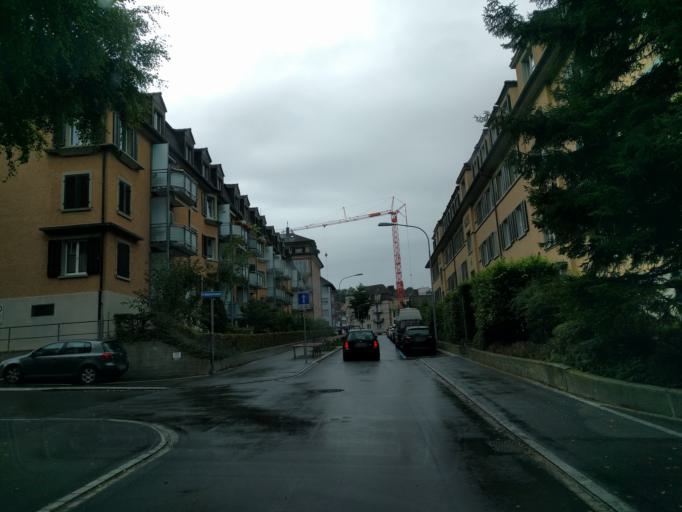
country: CH
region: Zurich
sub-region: Bezirk Zuerich
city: Zuerich (Kreis 7) / Hirslanden
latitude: 47.3595
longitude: 8.5675
